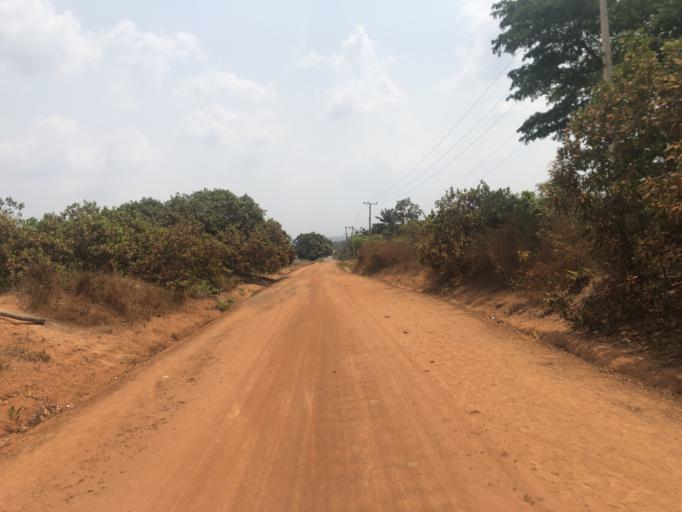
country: NG
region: Osun
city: Bode Osi
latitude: 7.7816
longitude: 4.1971
